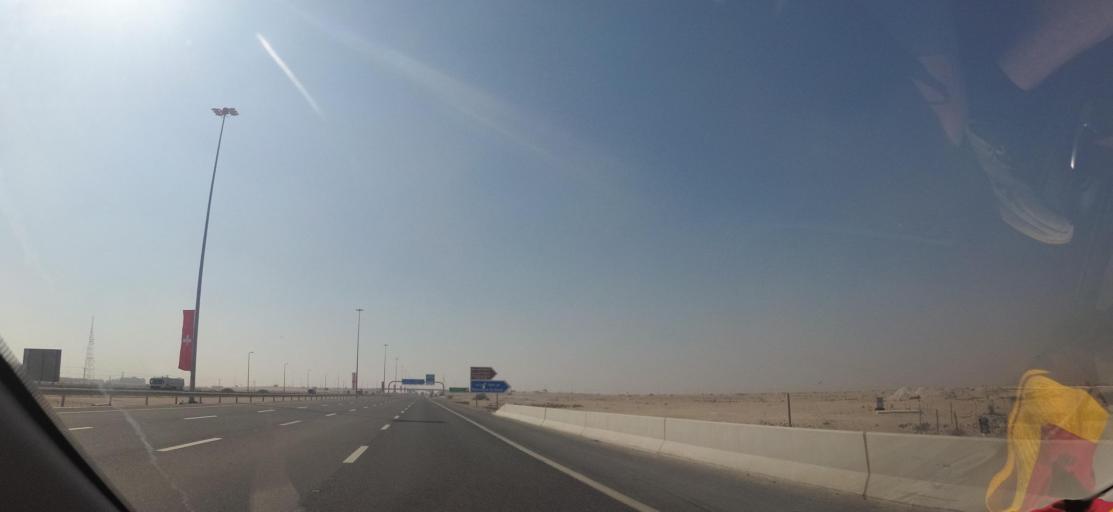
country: QA
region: Baladiyat ar Rayyan
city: Ash Shahaniyah
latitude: 25.1140
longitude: 51.1762
